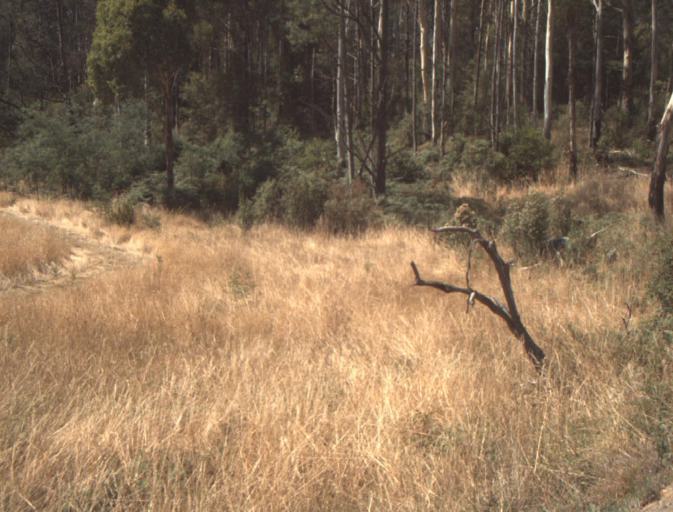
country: AU
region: Tasmania
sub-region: Launceston
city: Mayfield
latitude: -41.2558
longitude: 147.1864
